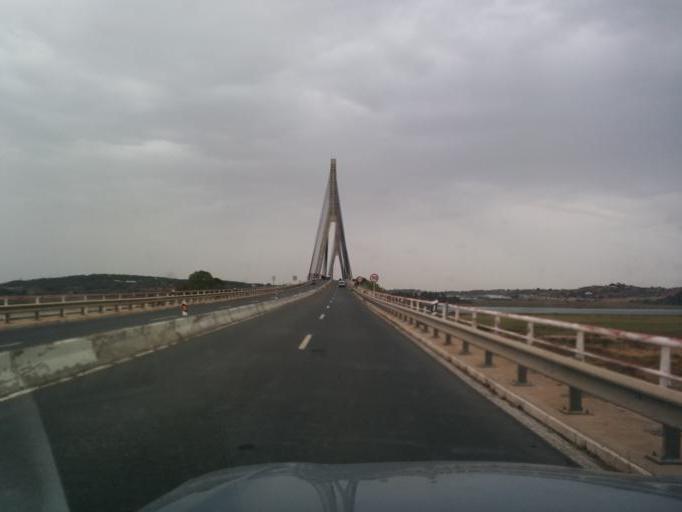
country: PT
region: Faro
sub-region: Castro Marim
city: Castro Marim
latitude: 37.2376
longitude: -7.4262
